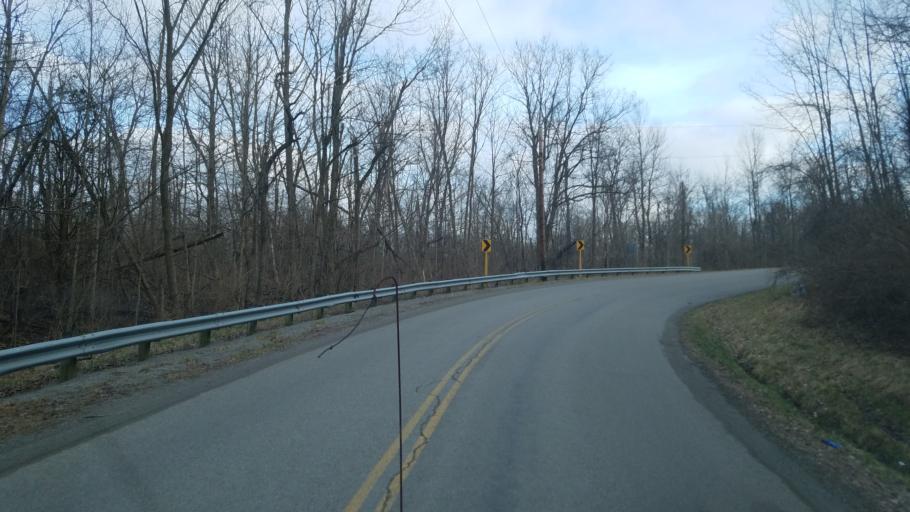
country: US
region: Ohio
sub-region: Logan County
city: Bellefontaine
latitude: 40.3202
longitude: -83.6620
